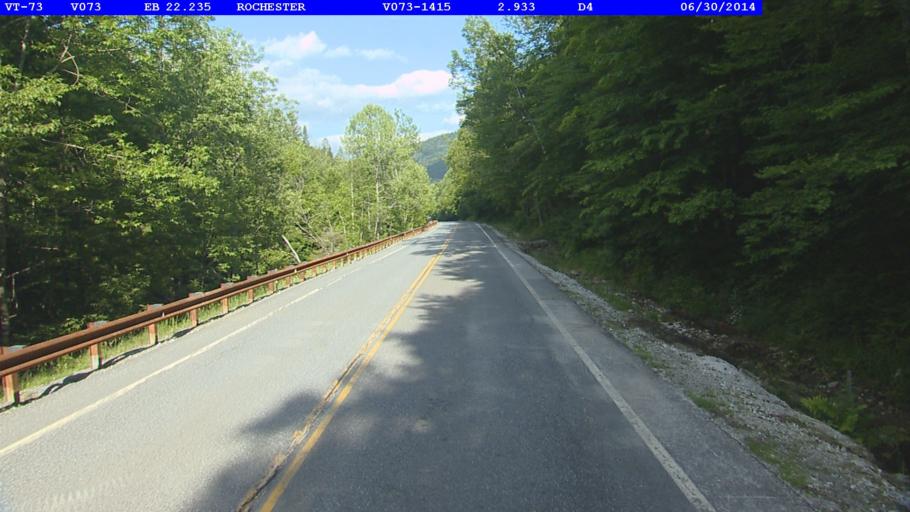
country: US
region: Vermont
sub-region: Rutland County
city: Brandon
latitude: 43.8535
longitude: -72.9120
